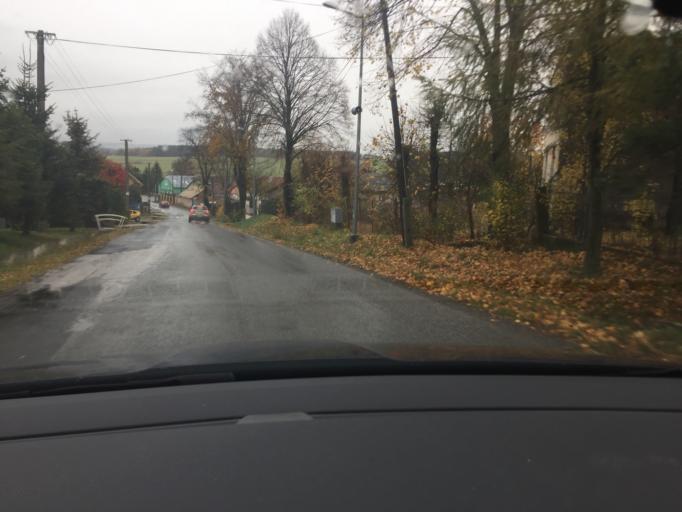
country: SK
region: Presovsky
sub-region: Okres Presov
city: Kezmarok
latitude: 49.1896
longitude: 20.3866
